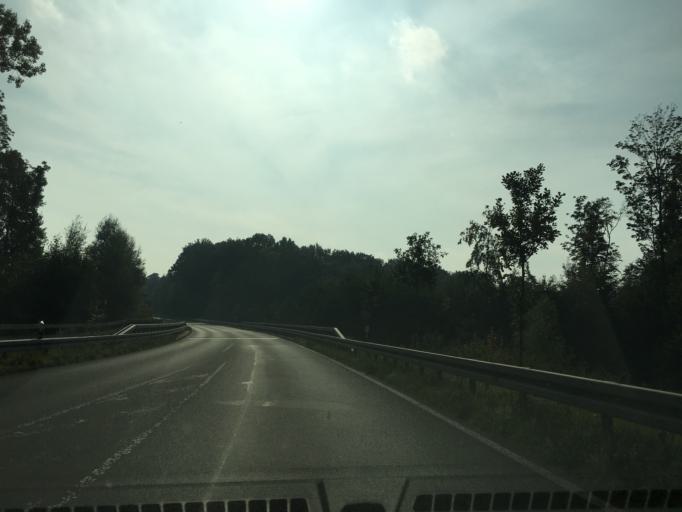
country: DE
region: North Rhine-Westphalia
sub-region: Regierungsbezirk Munster
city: Dulmen
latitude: 51.7979
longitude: 7.3366
